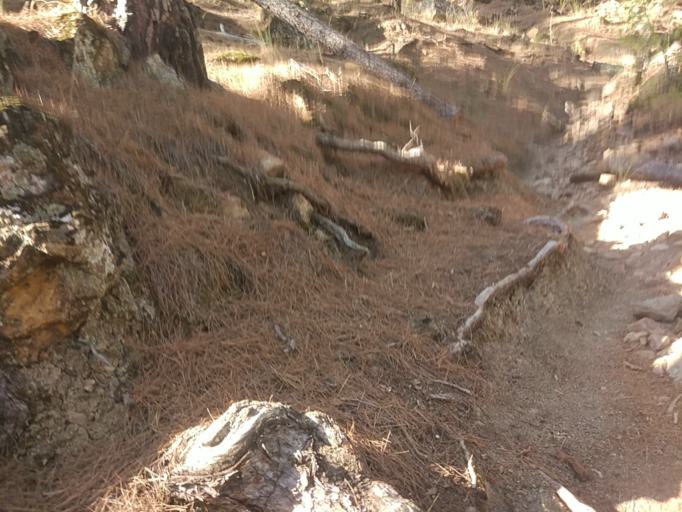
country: TR
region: Antalya
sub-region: Kemer
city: Goeynuek
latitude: 36.6773
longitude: 30.4937
